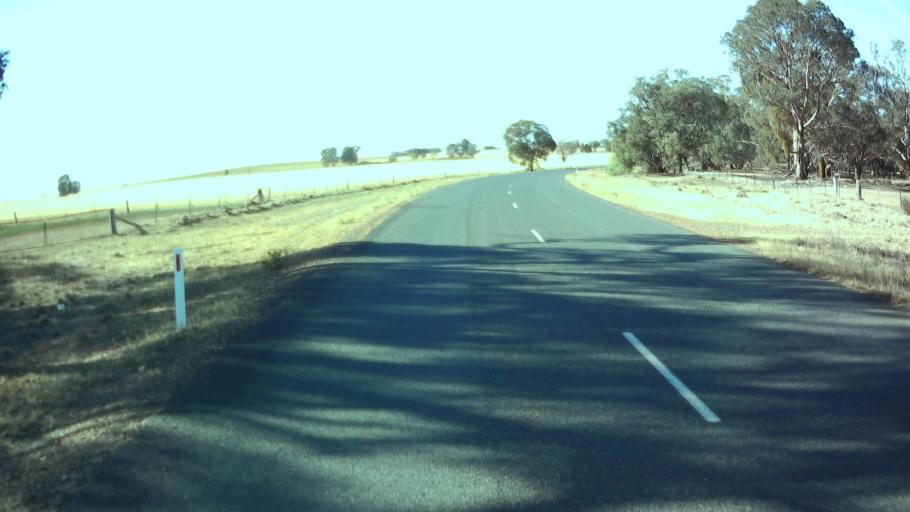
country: AU
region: New South Wales
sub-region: Weddin
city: Grenfell
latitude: -33.9847
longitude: 148.1408
